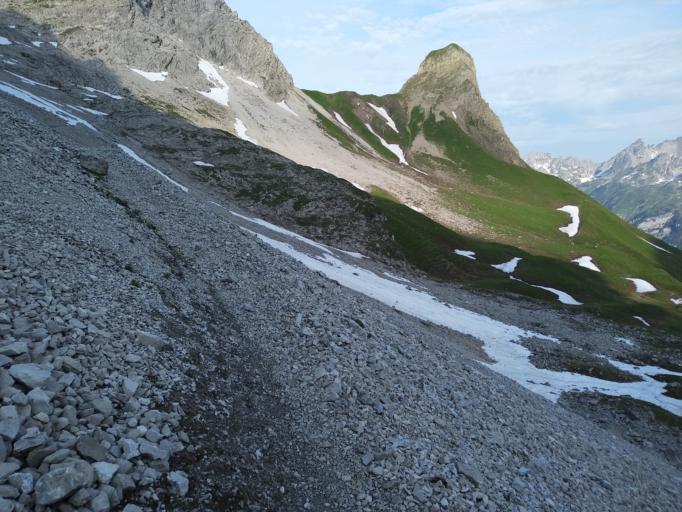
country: AT
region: Tyrol
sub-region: Politischer Bezirk Reutte
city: Steeg
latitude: 47.2838
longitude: 10.2534
